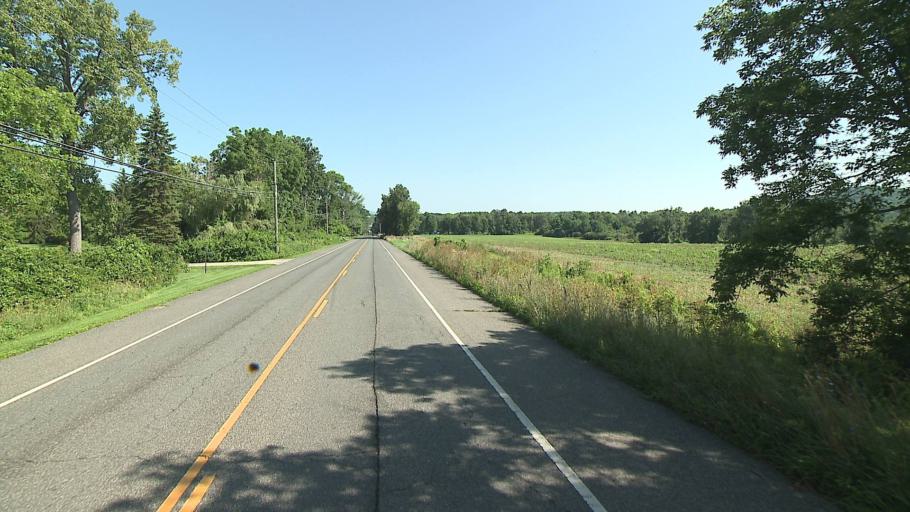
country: US
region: Connecticut
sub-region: Litchfield County
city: Canaan
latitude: 41.9055
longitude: -73.4473
